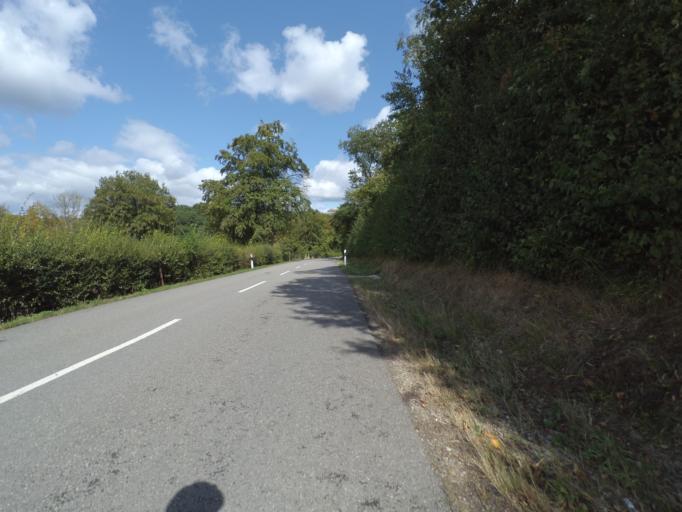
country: LU
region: Grevenmacher
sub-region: Canton de Grevenmacher
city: Flaxweiler
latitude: 49.6355
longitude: 6.3357
